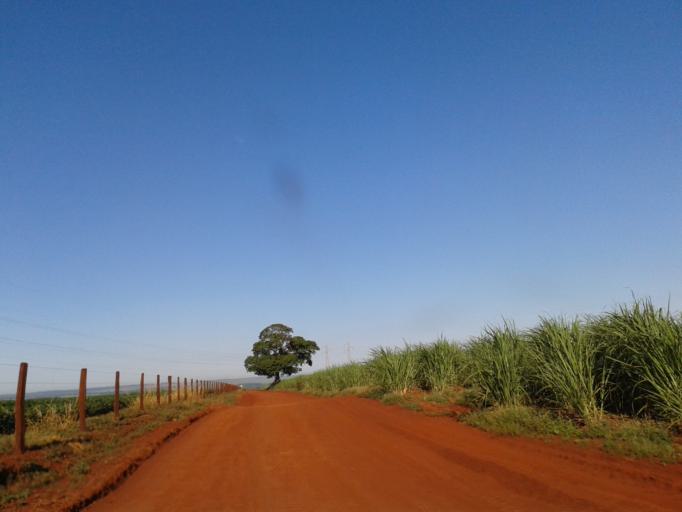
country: BR
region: Minas Gerais
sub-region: Centralina
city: Centralina
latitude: -18.6708
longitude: -49.2839
